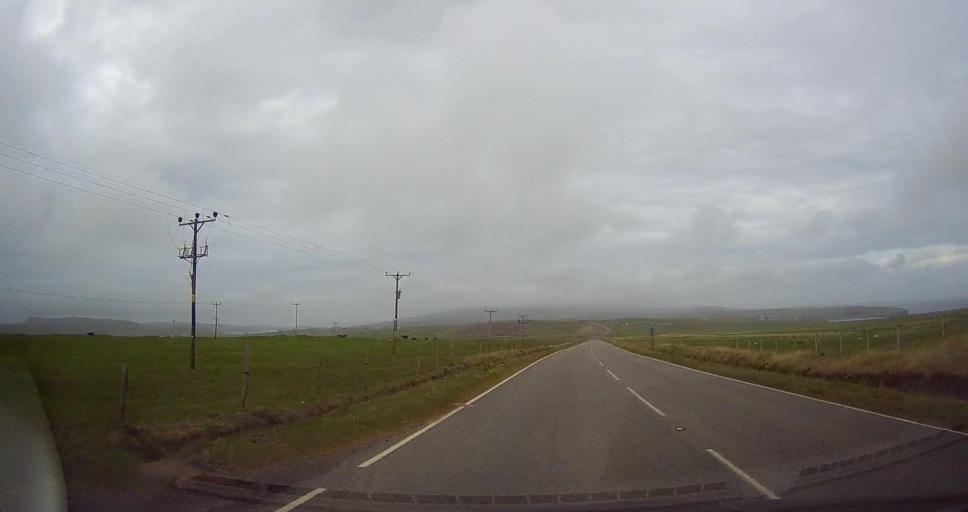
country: GB
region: Scotland
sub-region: Shetland Islands
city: Sandwick
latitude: 59.8980
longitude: -1.3036
